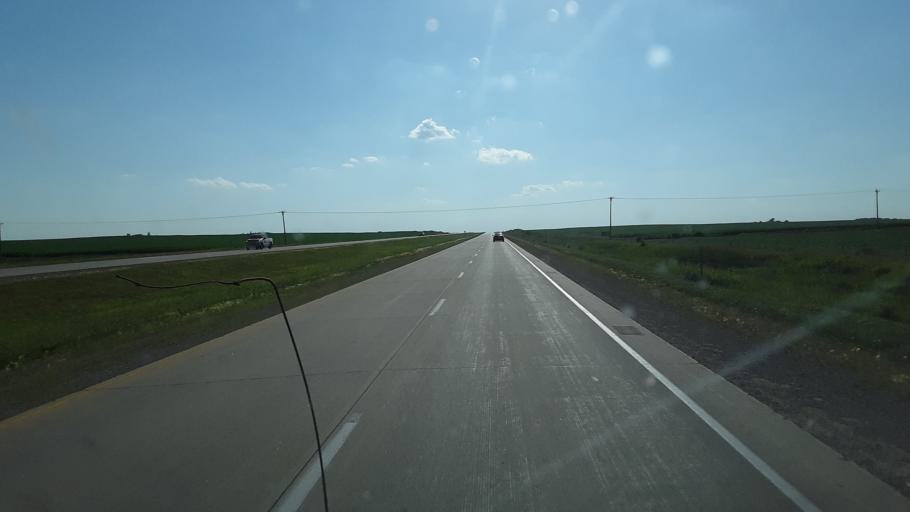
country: US
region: Iowa
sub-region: Grundy County
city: Dike
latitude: 42.4638
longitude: -92.6881
